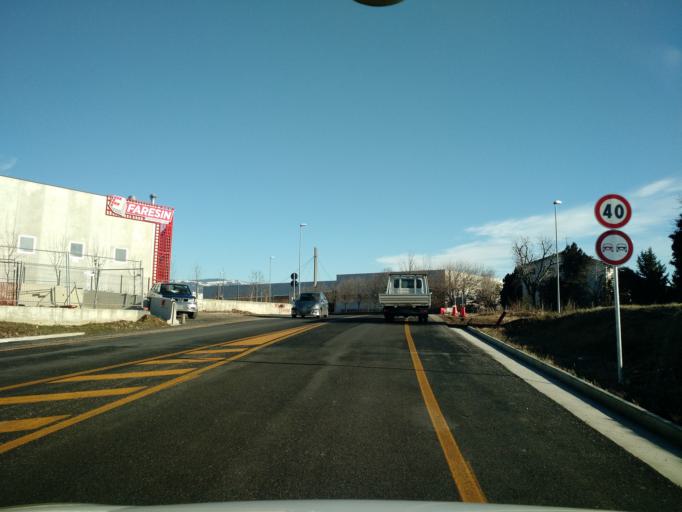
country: IT
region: Veneto
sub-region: Provincia di Vicenza
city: Breganze
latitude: 45.6962
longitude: 11.5511
